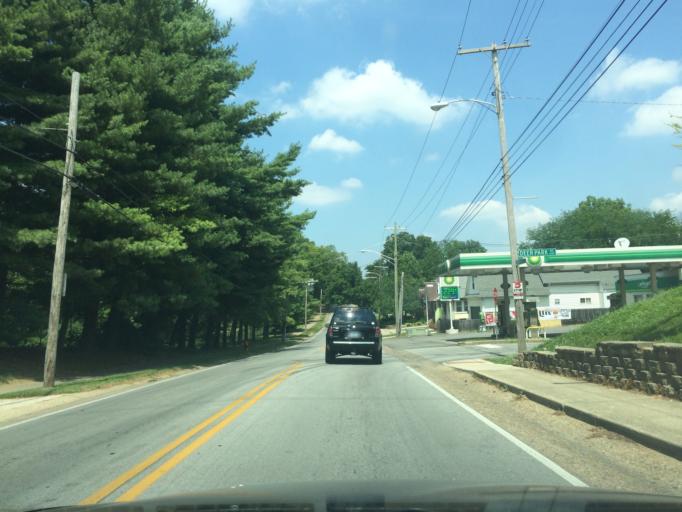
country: US
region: Kentucky
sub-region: Jefferson County
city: Audubon Park
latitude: 38.2238
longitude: -85.7112
